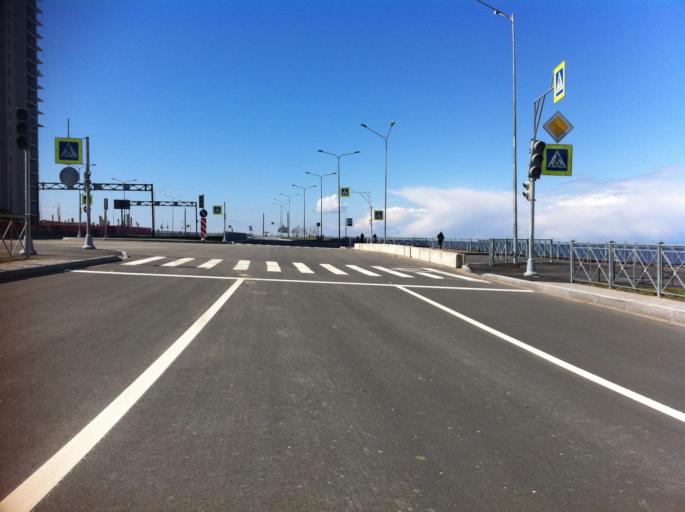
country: RU
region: St.-Petersburg
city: Uritsk
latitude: 59.8704
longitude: 30.1611
